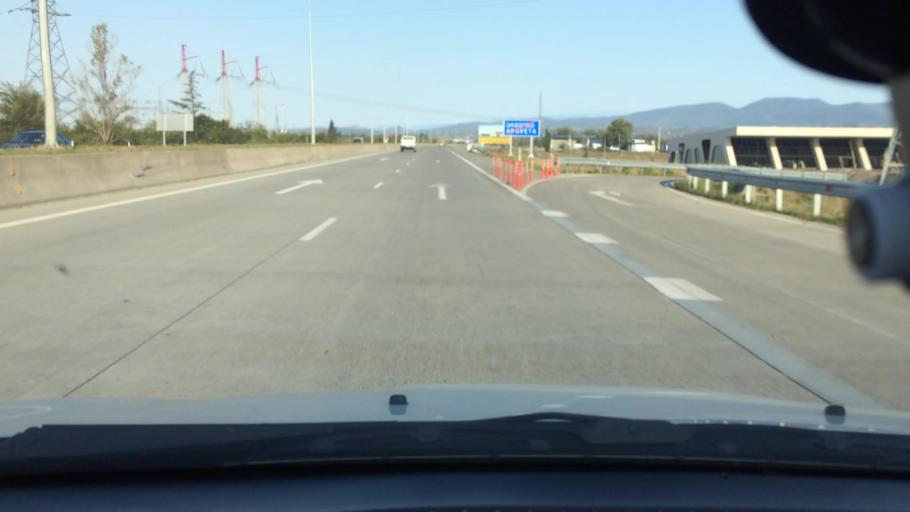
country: GE
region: Imereti
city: Zestap'oni
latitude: 42.1462
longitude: 42.9660
